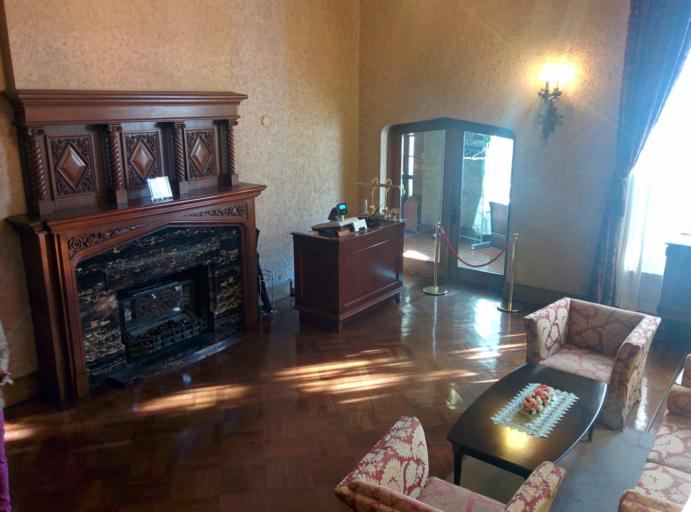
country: JP
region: Osaka
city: Ikeda
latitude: 34.8243
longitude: 135.4308
